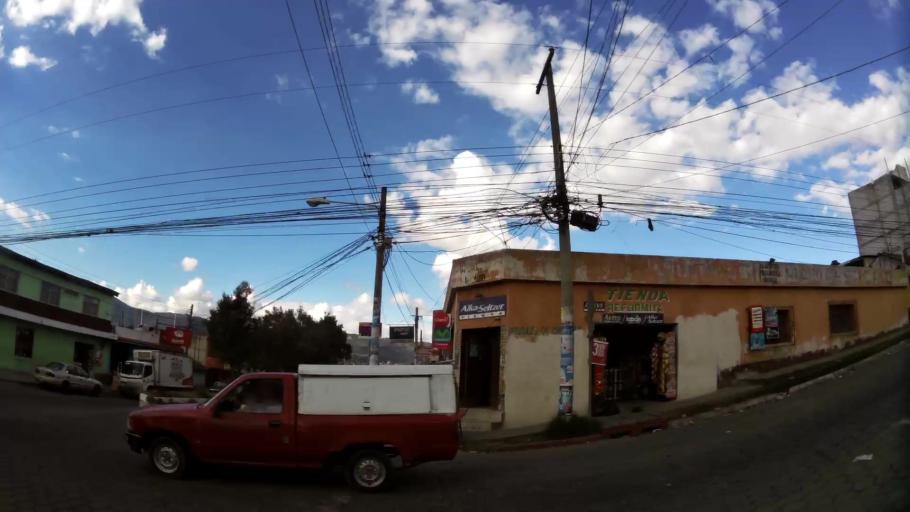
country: GT
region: Quetzaltenango
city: Quetzaltenango
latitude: 14.8477
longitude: -91.5187
